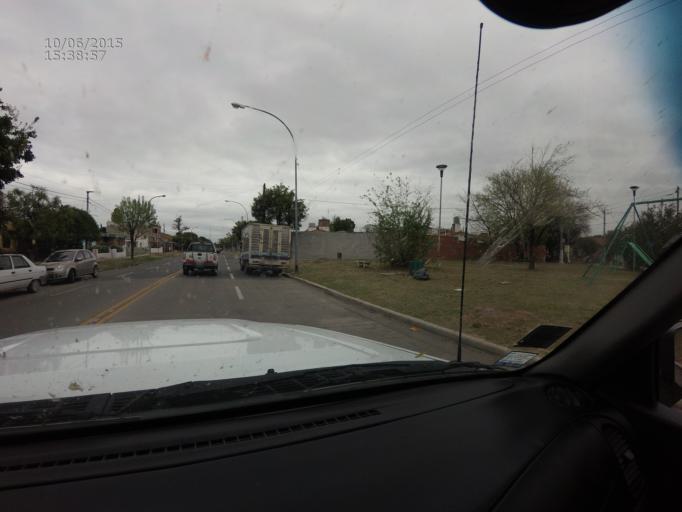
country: AR
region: Cordoba
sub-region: Departamento de Capital
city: Cordoba
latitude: -31.3607
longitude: -64.2262
